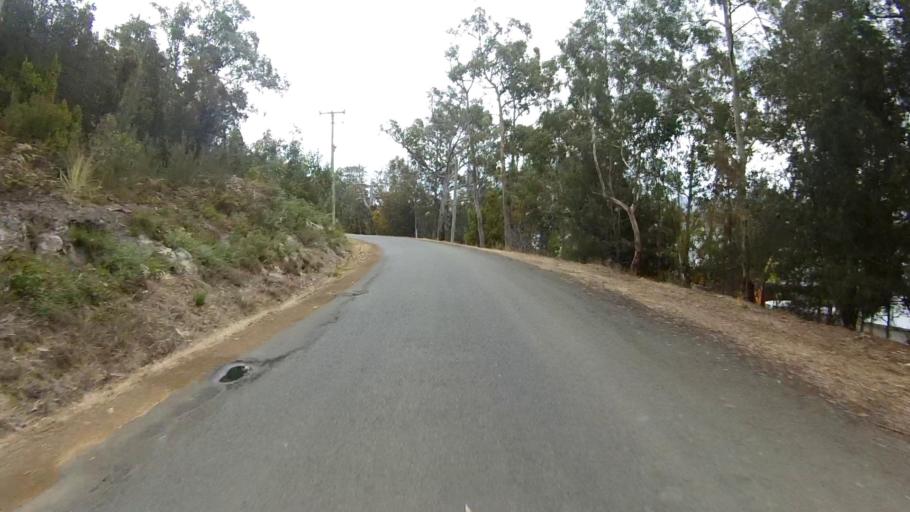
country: AU
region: Tasmania
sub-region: Huon Valley
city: Cygnet
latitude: -43.2172
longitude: 147.0969
